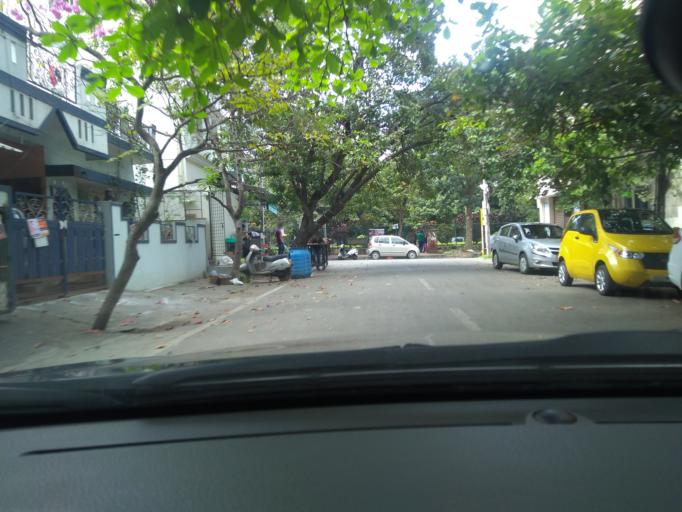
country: IN
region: Karnataka
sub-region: Bangalore Urban
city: Bangalore
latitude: 13.0037
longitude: 77.6609
